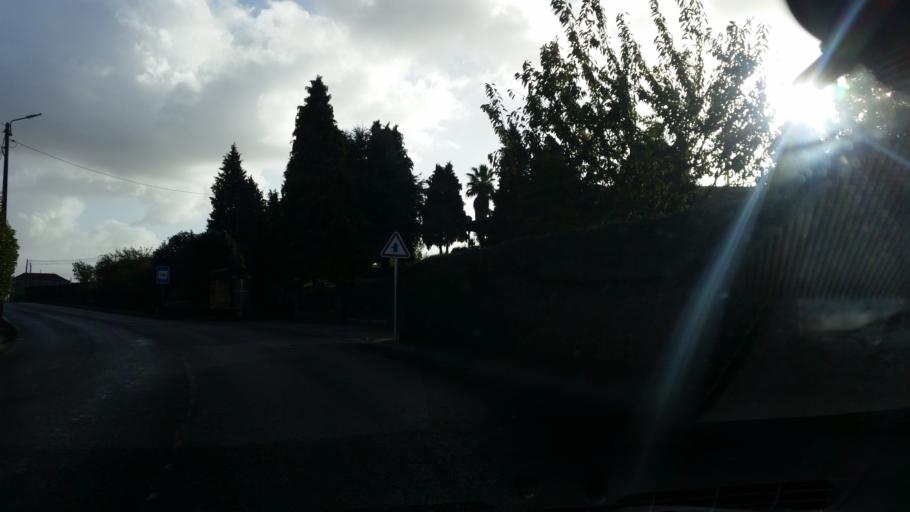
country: PT
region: Porto
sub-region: Santo Tirso
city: Aves
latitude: 41.3551
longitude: -8.4280
